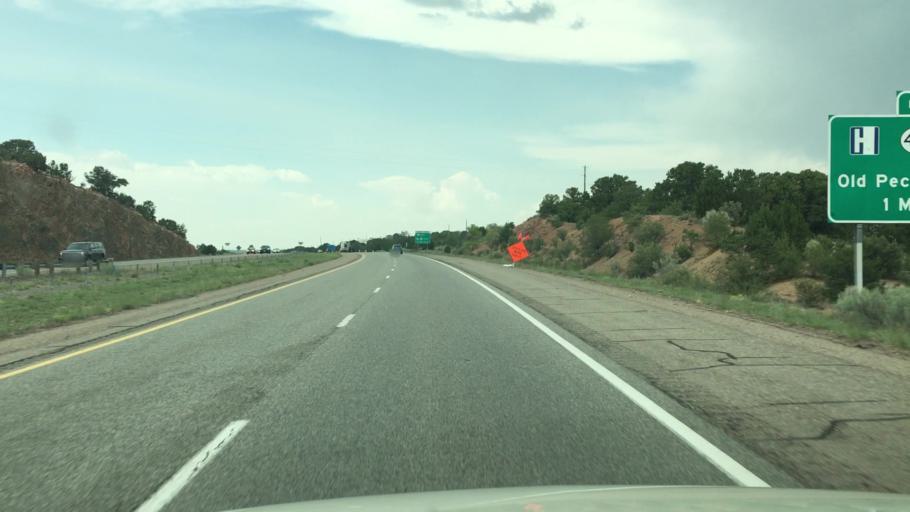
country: US
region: New Mexico
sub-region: Santa Fe County
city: Santa Fe
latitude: 35.6225
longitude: -105.9198
